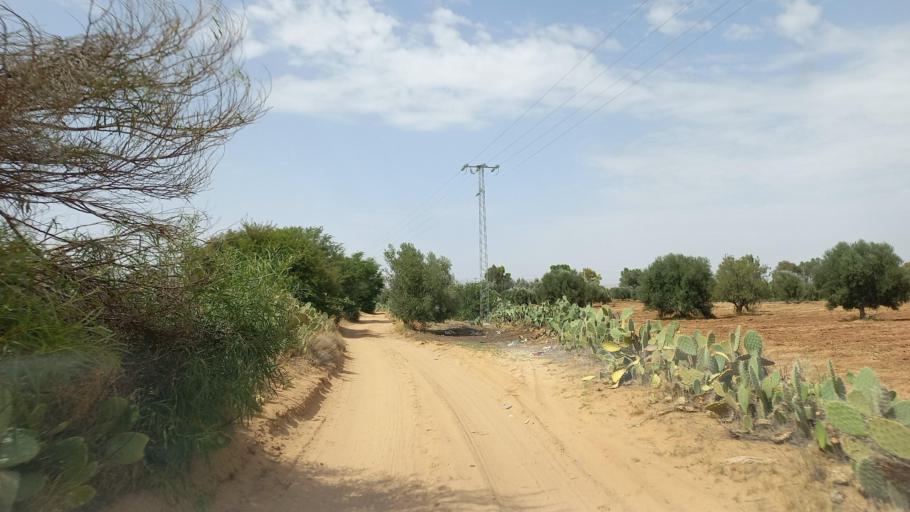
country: TN
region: Al Qasrayn
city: Kasserine
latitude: 35.2609
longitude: 9.0520
